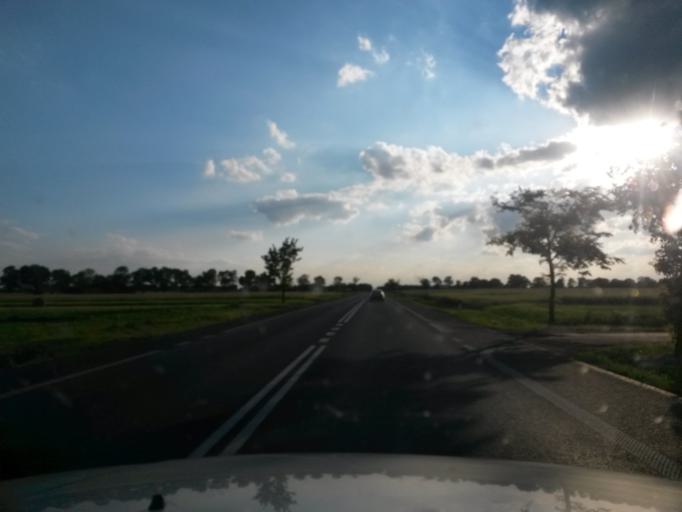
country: PL
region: Lodz Voivodeship
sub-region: Powiat belchatowski
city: Rusiec
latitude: 51.3149
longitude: 18.9320
